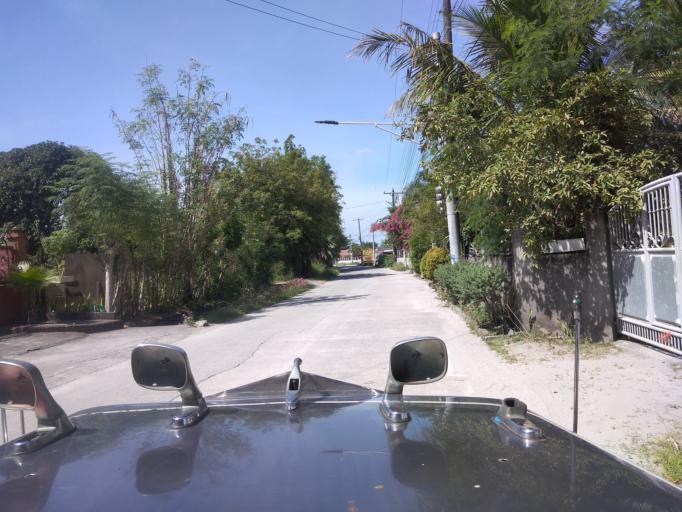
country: PH
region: Central Luzon
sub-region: Province of Pampanga
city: Bacolor
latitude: 15.0166
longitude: 120.6595
